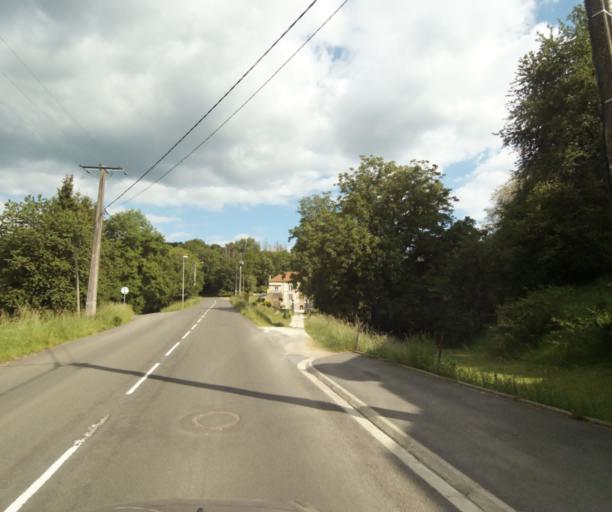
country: FR
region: Champagne-Ardenne
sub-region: Departement des Ardennes
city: Montcy-Notre-Dame
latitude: 49.7693
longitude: 4.7430
